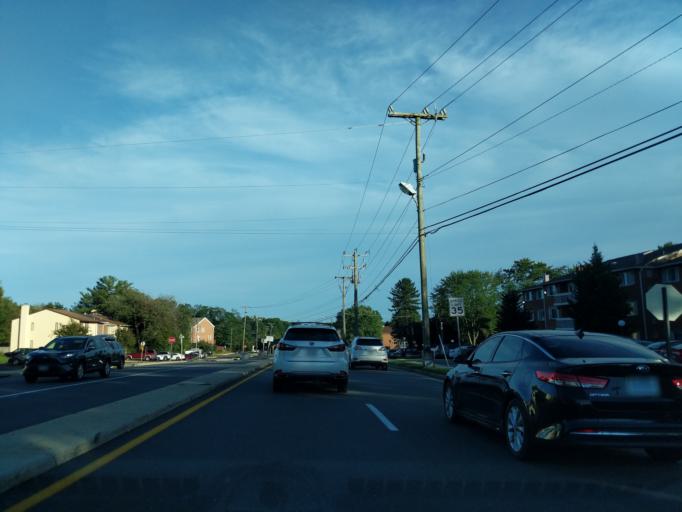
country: US
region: Virginia
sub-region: Fairfax County
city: Mantua
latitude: 38.8689
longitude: -77.2769
